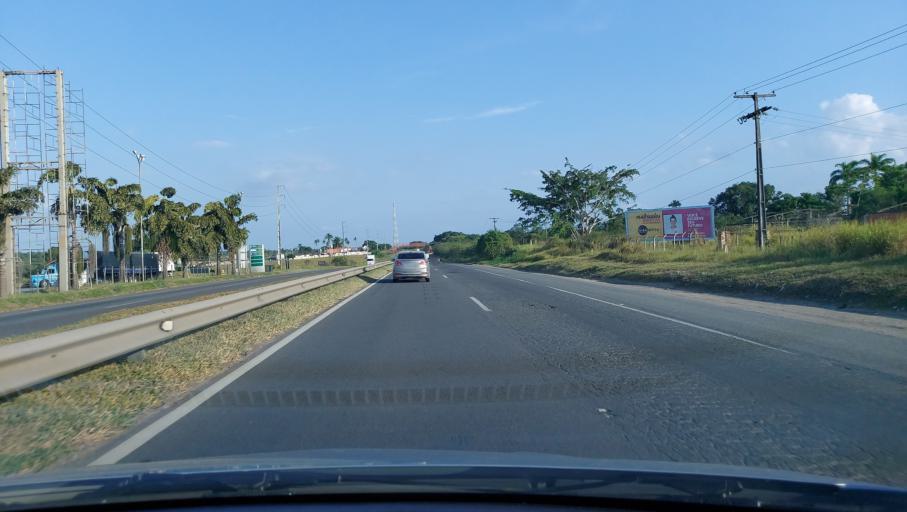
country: BR
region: Bahia
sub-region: Conceicao Do Jacuipe
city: Conceicao do Jacuipe
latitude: -12.3847
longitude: -38.7933
